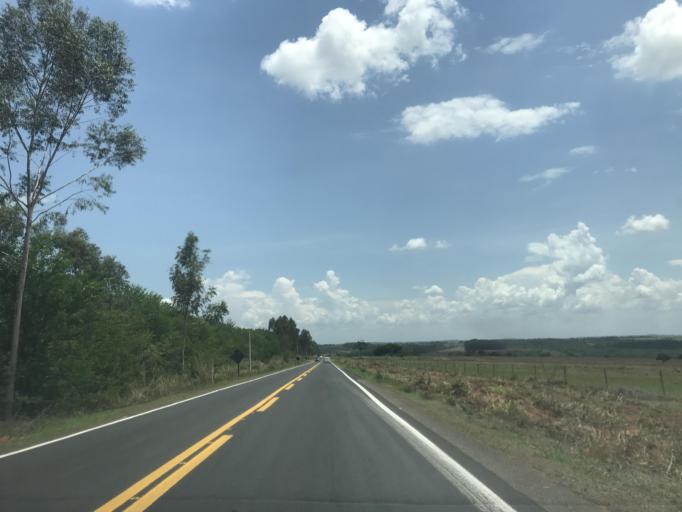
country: BR
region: Goias
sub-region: Bela Vista De Goias
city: Bela Vista de Goias
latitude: -17.1071
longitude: -48.6654
